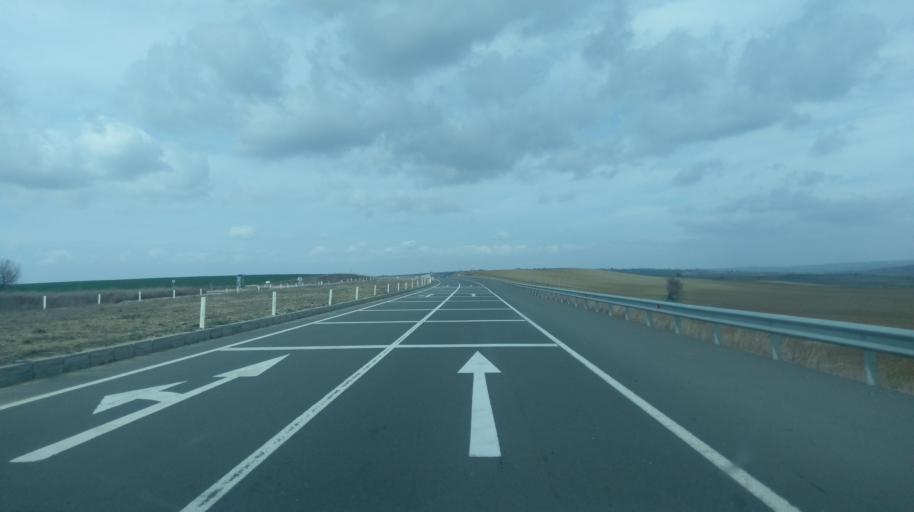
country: TR
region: Edirne
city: Hamidiye
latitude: 41.0254
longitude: 26.6355
